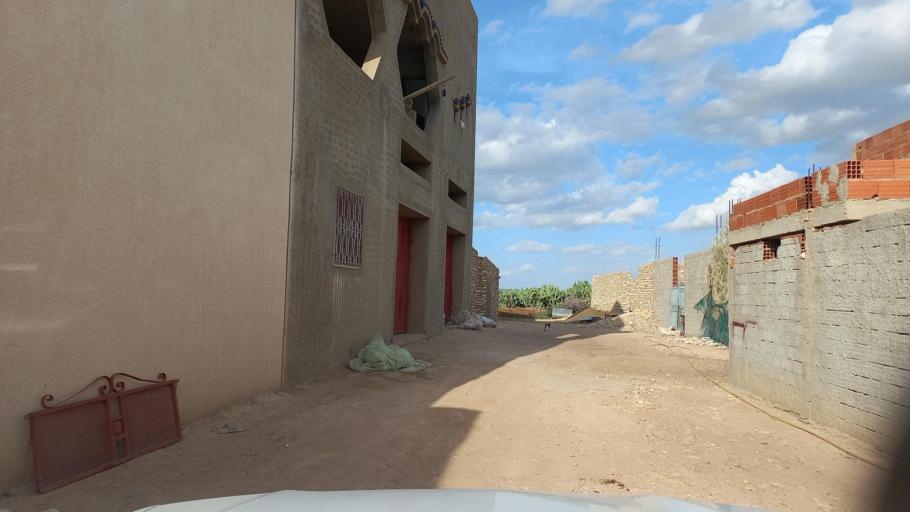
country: TN
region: Al Qasrayn
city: Sbiba
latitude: 35.4475
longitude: 9.0775
